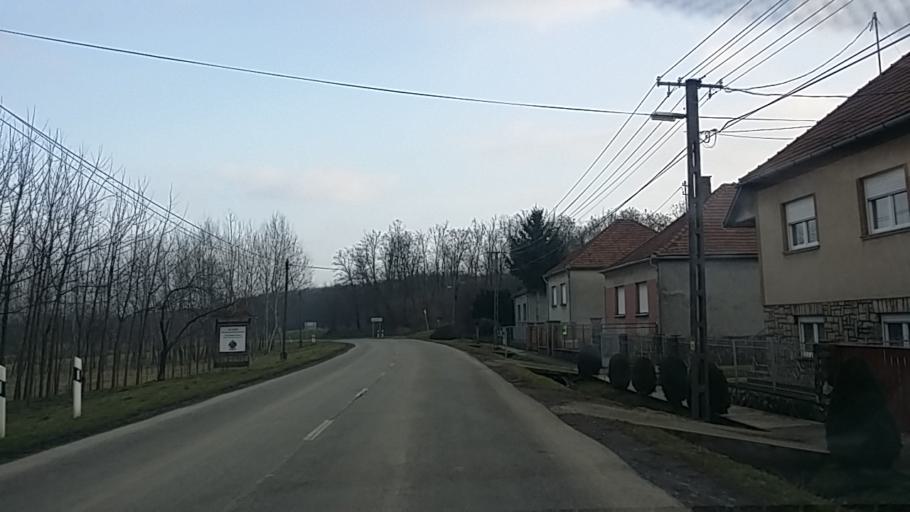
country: HU
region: Baranya
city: Lanycsok
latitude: 46.0420
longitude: 18.6067
